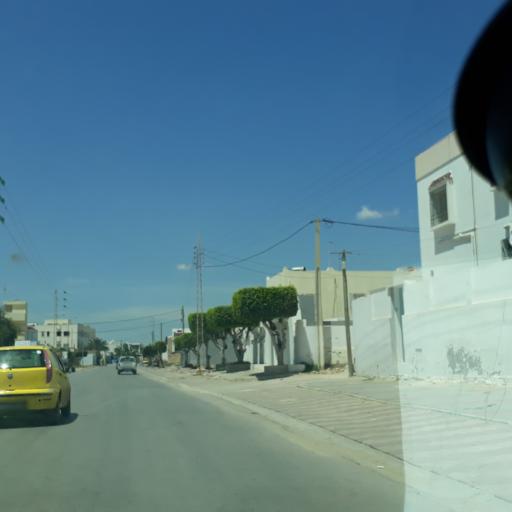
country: TN
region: Safaqis
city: Al Qarmadah
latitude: 34.8098
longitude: 10.7496
